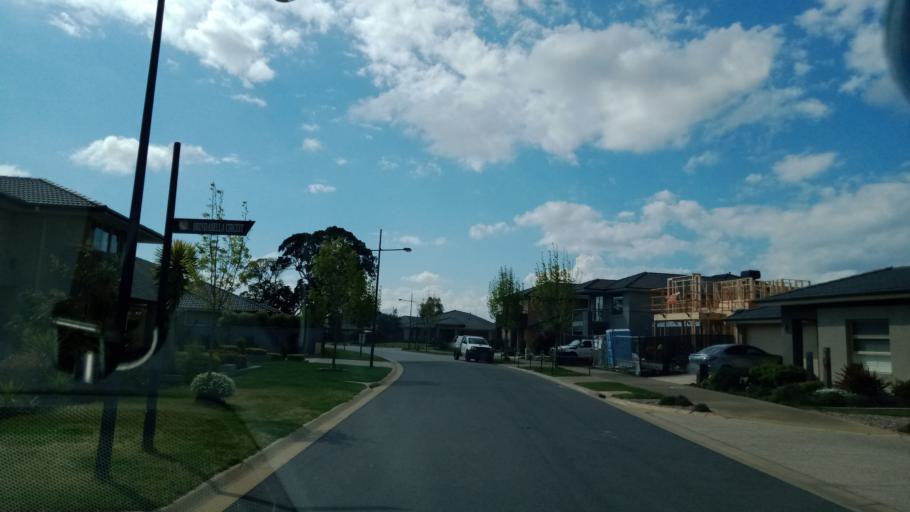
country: AU
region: Victoria
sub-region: Frankston
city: Sandhurst
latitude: -38.0874
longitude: 145.2081
